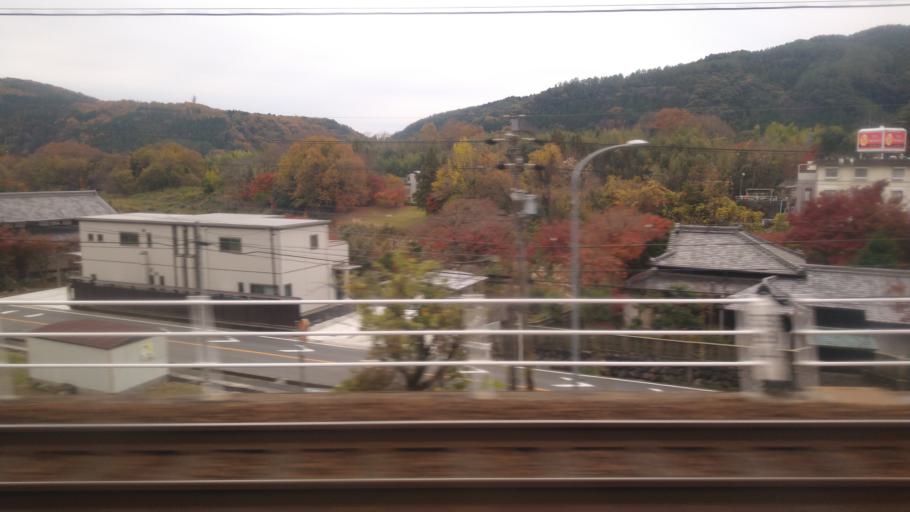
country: JP
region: Aichi
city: Seto
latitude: 35.2663
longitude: 137.0560
